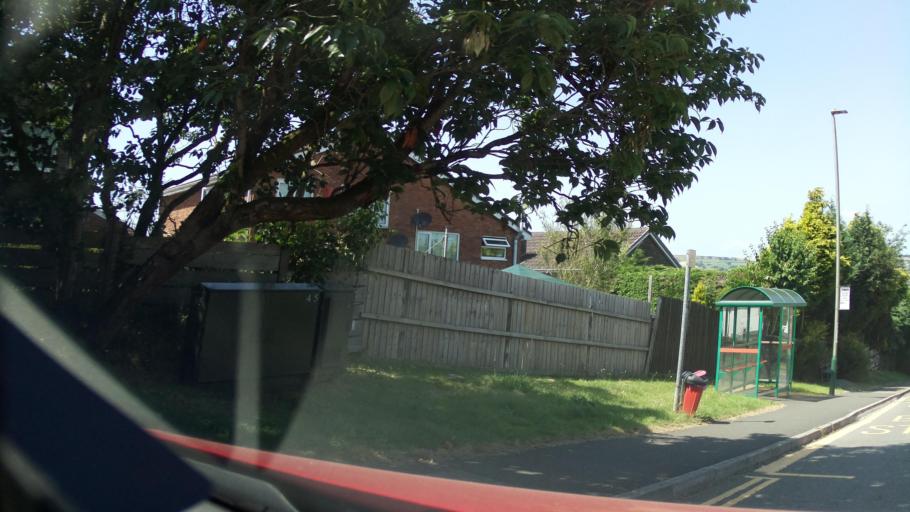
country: GB
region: Wales
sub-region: Caerphilly County Borough
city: Caerphilly
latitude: 51.5678
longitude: -3.2308
